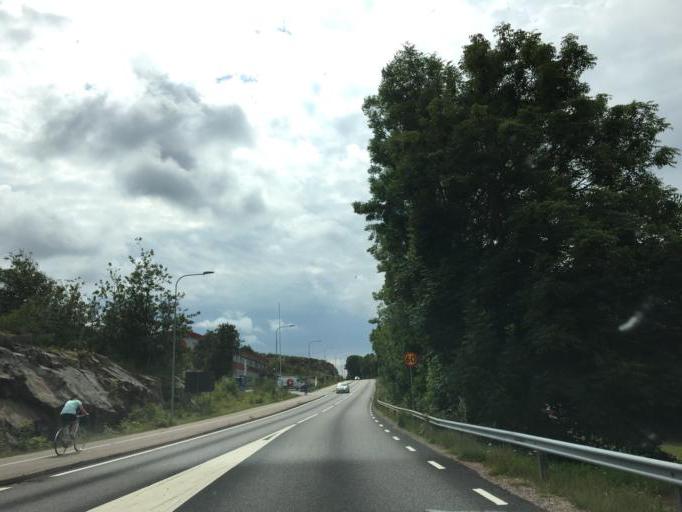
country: SE
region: Vaestra Goetaland
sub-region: Sotenas Kommun
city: Kungshamn
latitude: 58.3735
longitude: 11.2532
